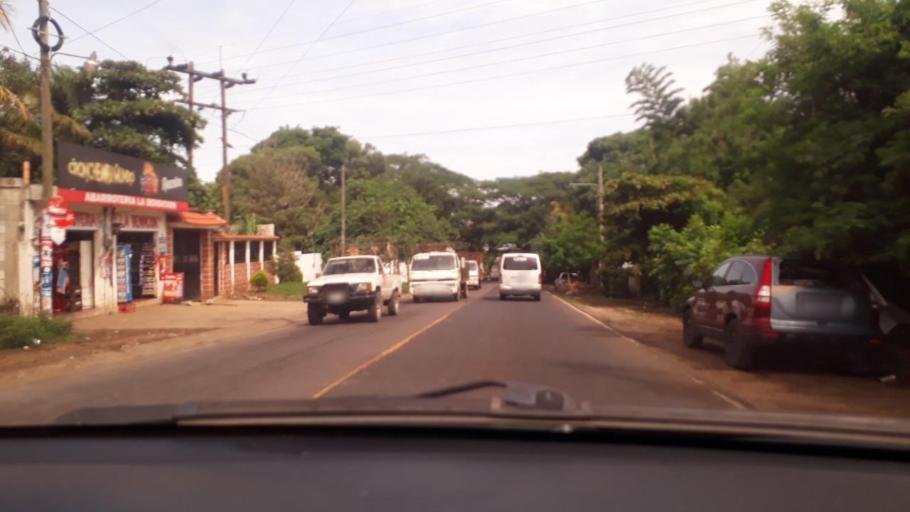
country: GT
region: Jutiapa
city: Quesada
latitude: 14.2746
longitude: -90.0000
